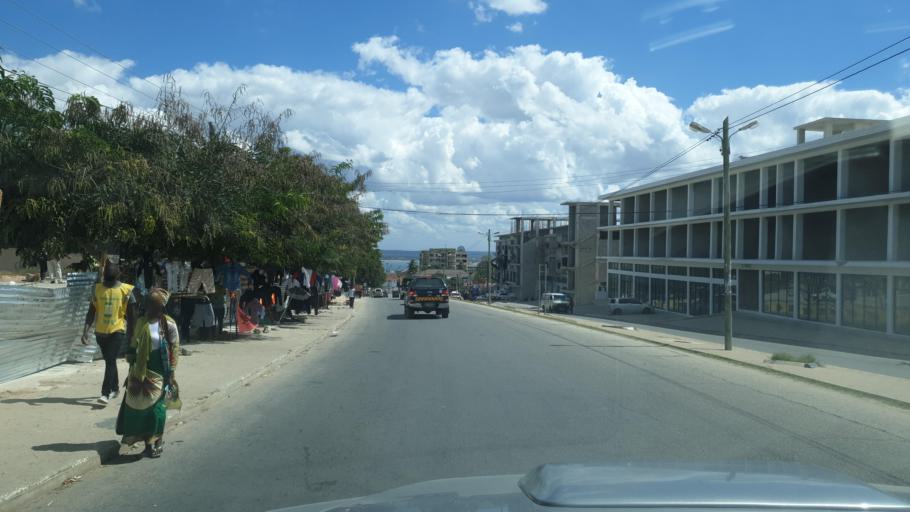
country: MZ
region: Nampula
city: Nacala
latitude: -14.5437
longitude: 40.6809
